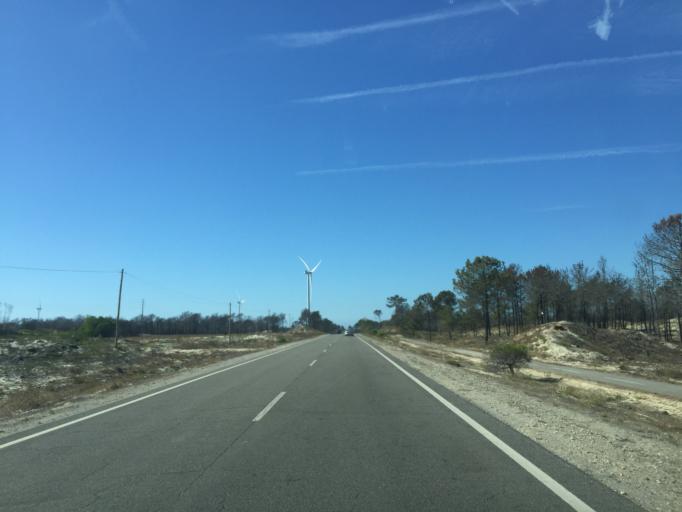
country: PT
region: Coimbra
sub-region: Mira
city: Mira
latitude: 40.3237
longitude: -8.7989
